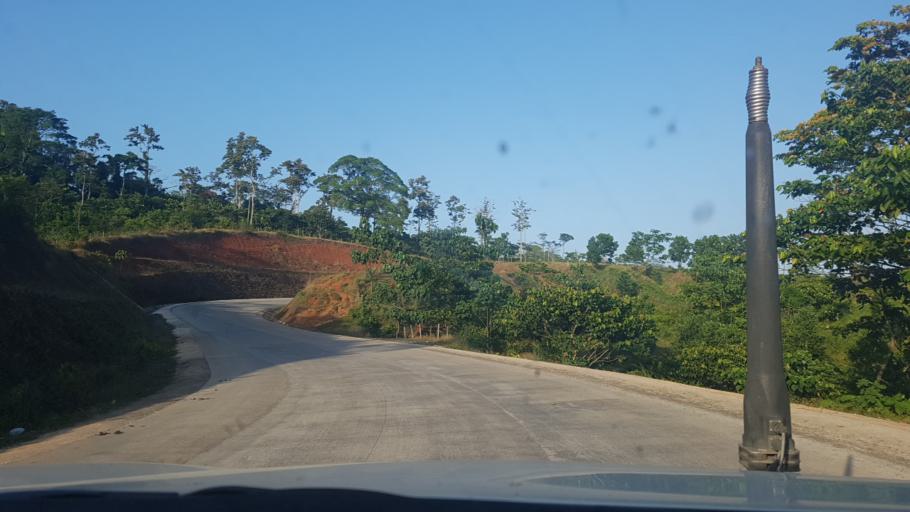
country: NI
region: Atlantico Sur
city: Nueva Guinea
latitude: 11.8055
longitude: -84.1170
